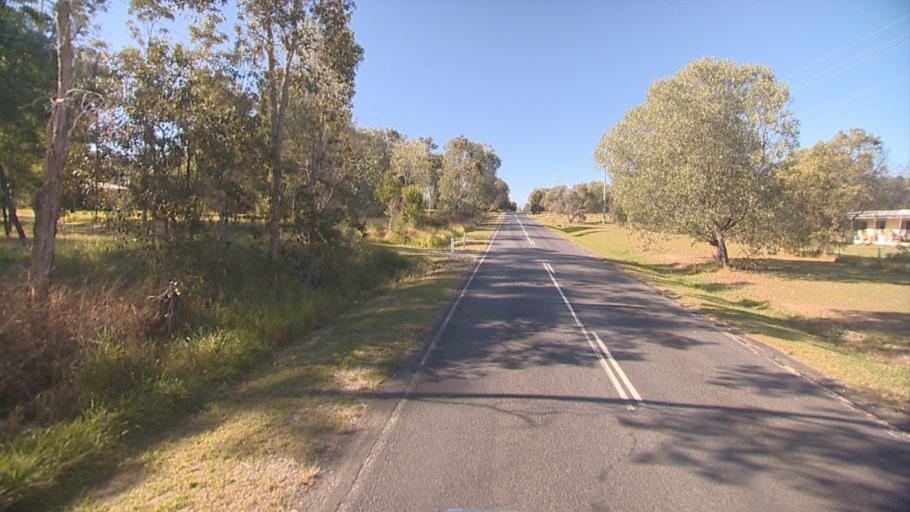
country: AU
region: Queensland
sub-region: Logan
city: North Maclean
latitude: -27.7843
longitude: 153.0510
